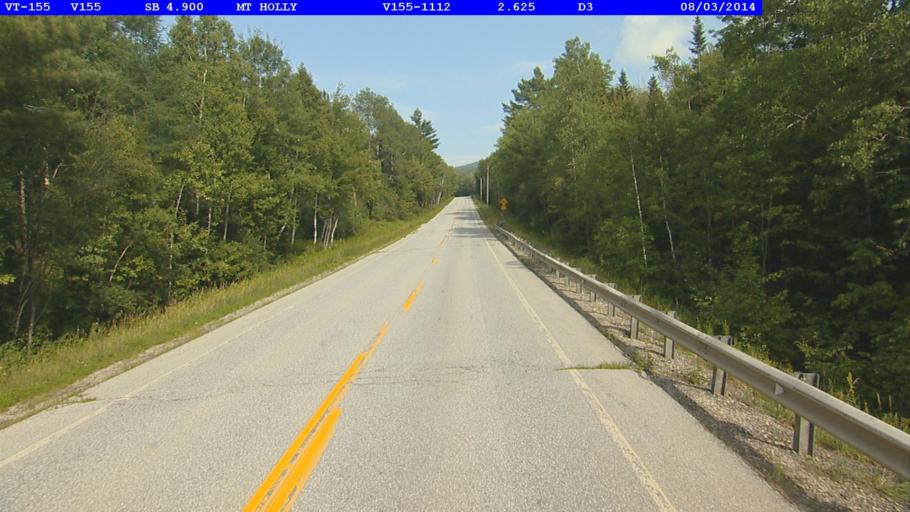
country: US
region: Vermont
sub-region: Windsor County
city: Chester
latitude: 43.3929
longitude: -72.8169
